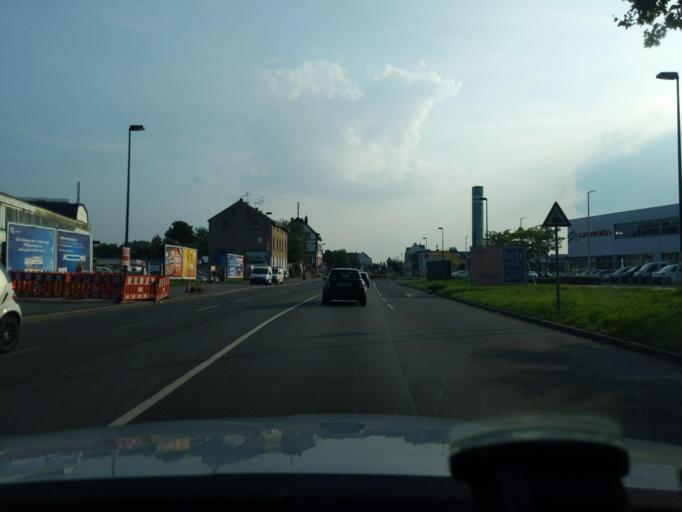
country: DE
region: North Rhine-Westphalia
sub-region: Regierungsbezirk Dusseldorf
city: Dusseldorf
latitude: 51.2208
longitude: 6.8220
